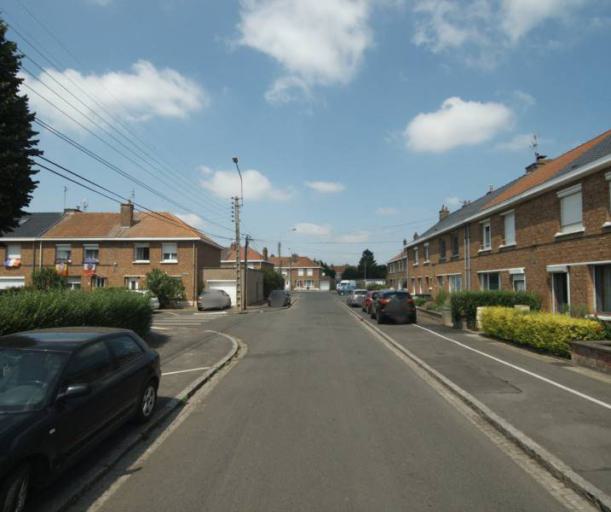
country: FR
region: Nord-Pas-de-Calais
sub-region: Departement du Nord
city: Armentieres
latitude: 50.6967
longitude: 2.8905
